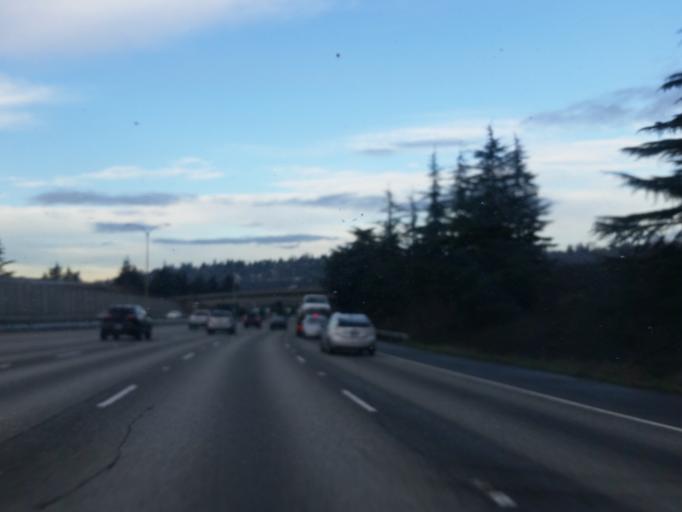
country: US
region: Washington
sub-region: King County
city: Tukwila
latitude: 47.4807
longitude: -122.2716
